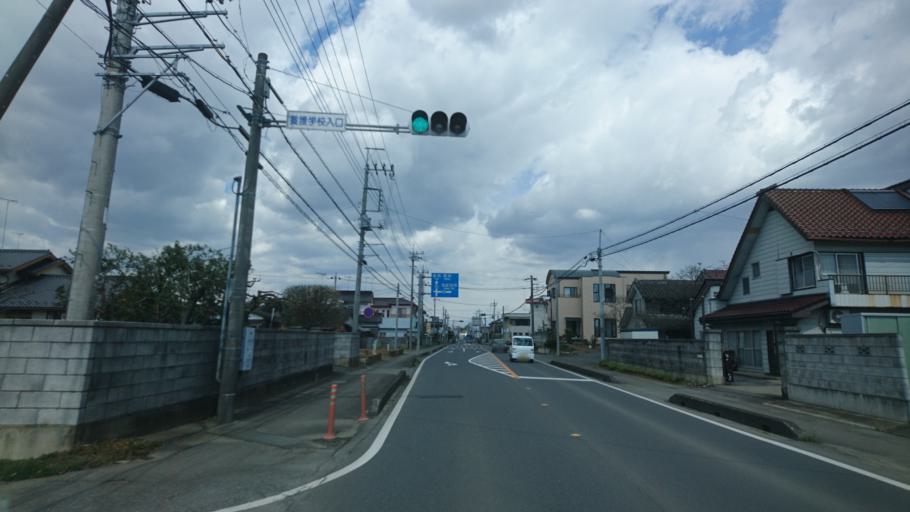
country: JP
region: Ibaraki
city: Shimodate
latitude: 36.2130
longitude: 139.9374
